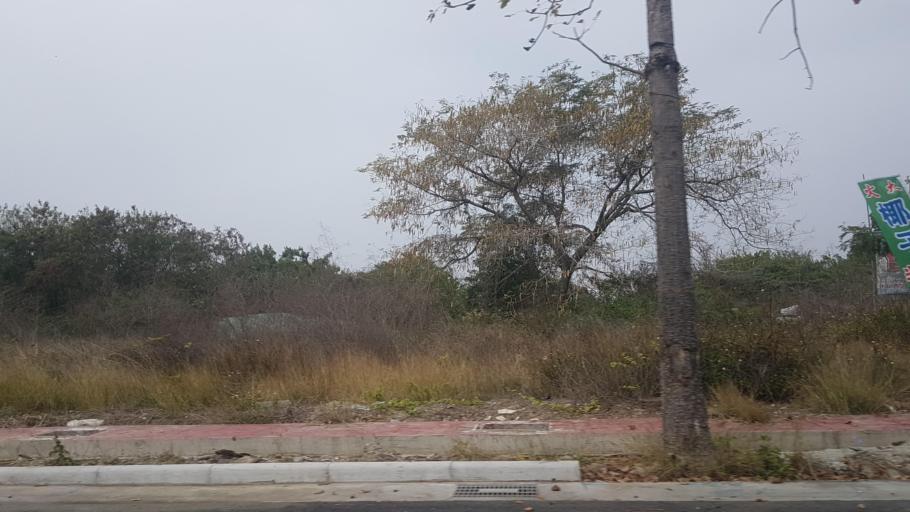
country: TW
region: Taiwan
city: Xinying
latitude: 23.3146
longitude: 120.3012
